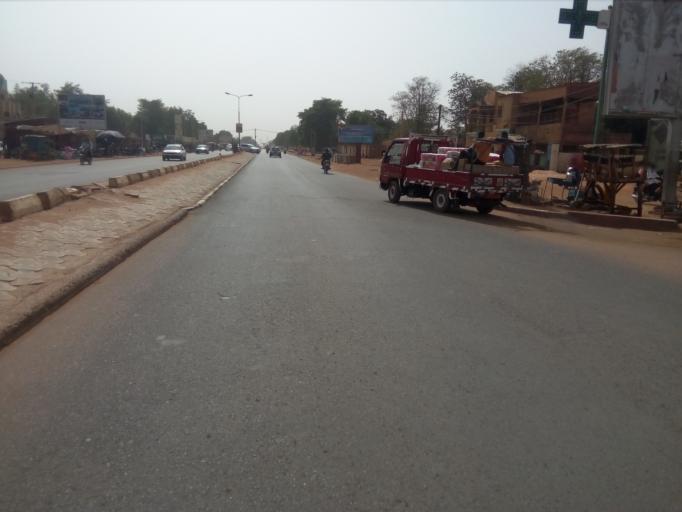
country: NE
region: Niamey
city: Niamey
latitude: 13.5343
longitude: 2.1034
